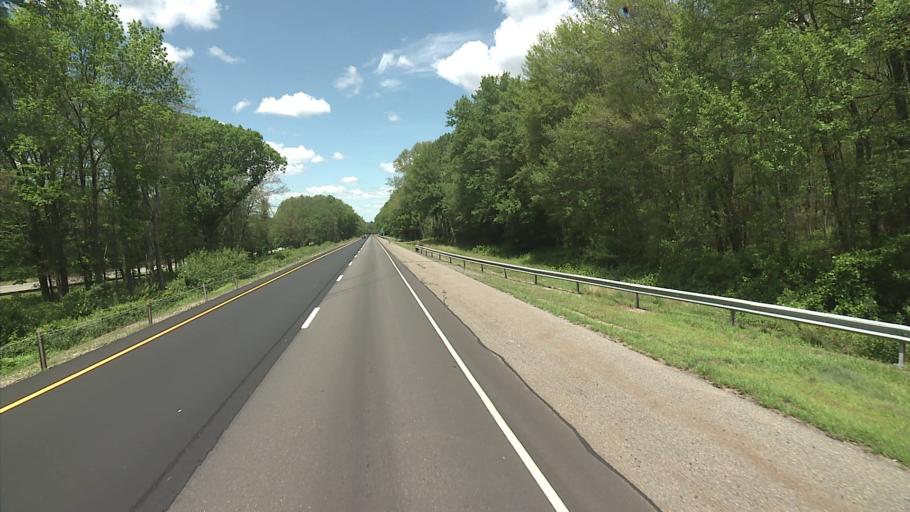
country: US
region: Connecticut
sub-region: Windham County
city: Killingly Center
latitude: 41.8222
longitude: -71.8709
